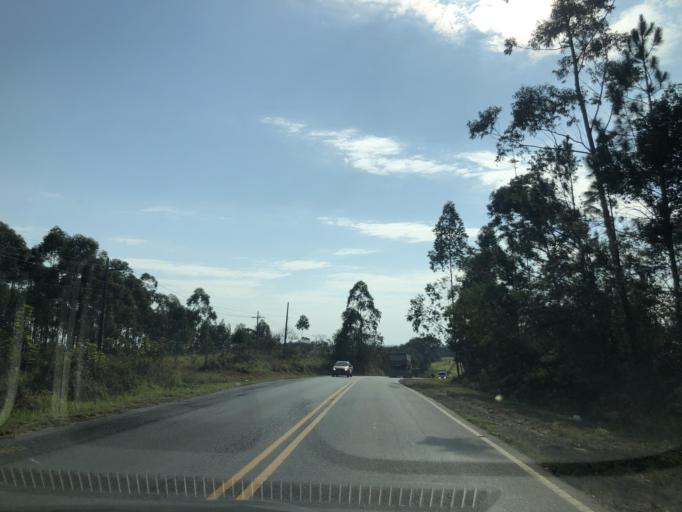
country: BR
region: Sao Paulo
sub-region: Pilar Do Sul
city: Pilar do Sul
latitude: -23.8120
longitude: -47.6869
